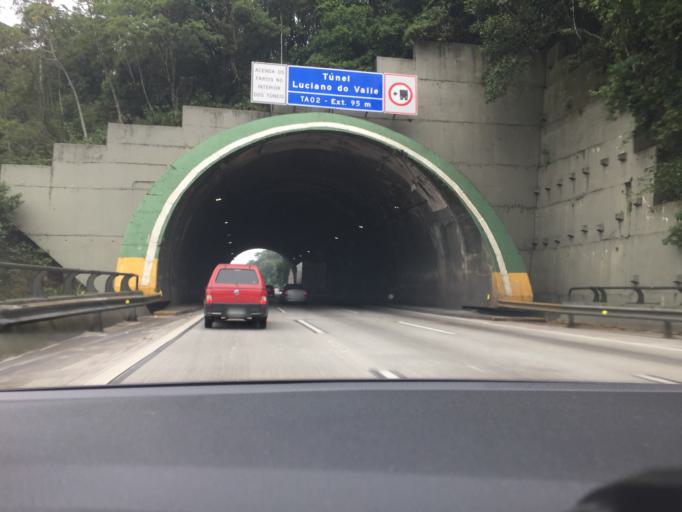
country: BR
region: Sao Paulo
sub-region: Cubatao
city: Cubatao
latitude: -23.9201
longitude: -46.5317
